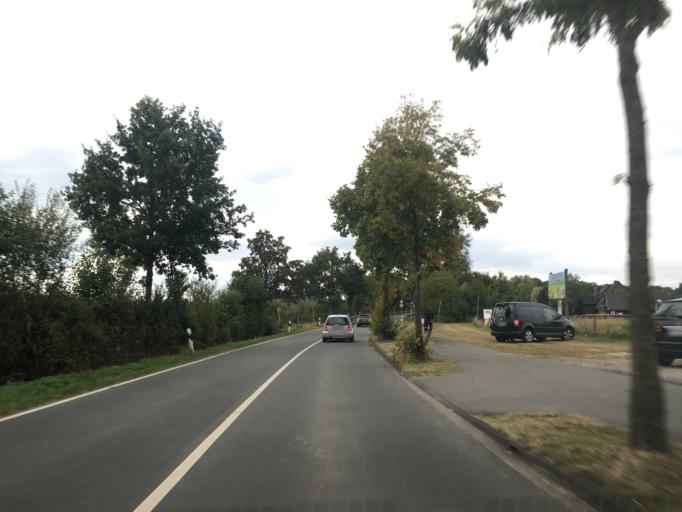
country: DE
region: North Rhine-Westphalia
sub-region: Regierungsbezirk Munster
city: Muenster
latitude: 51.9786
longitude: 7.5554
